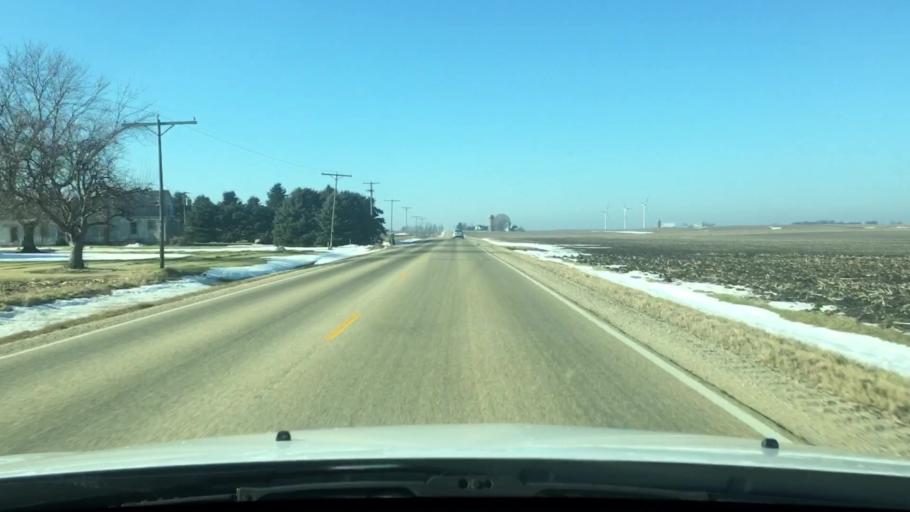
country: US
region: Illinois
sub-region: DeKalb County
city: Malta
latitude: 41.8487
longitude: -88.8998
